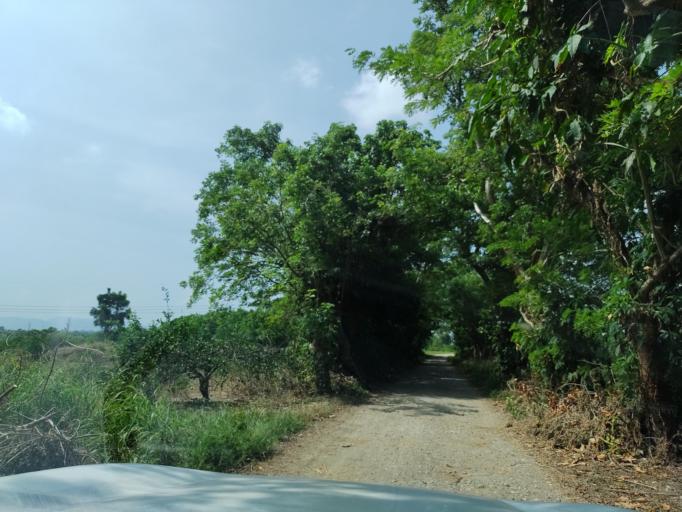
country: MX
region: Veracruz
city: Martinez de la Torre
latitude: 20.0907
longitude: -97.0466
